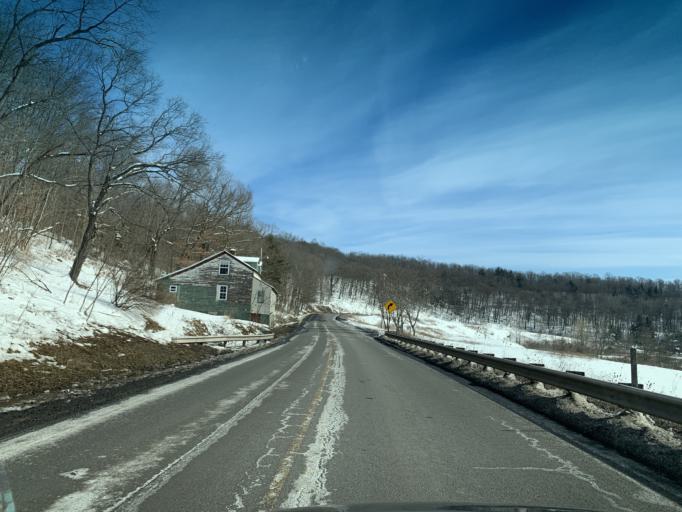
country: US
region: Maryland
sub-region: Allegany County
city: Lonaconing
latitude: 39.5977
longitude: -78.9456
